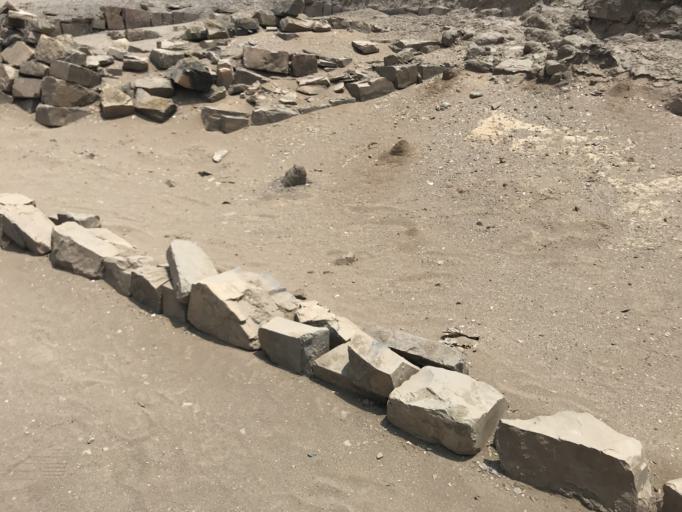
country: PE
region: Lima
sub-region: Lima
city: Punta Hermosa
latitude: -12.2631
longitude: -76.9024
